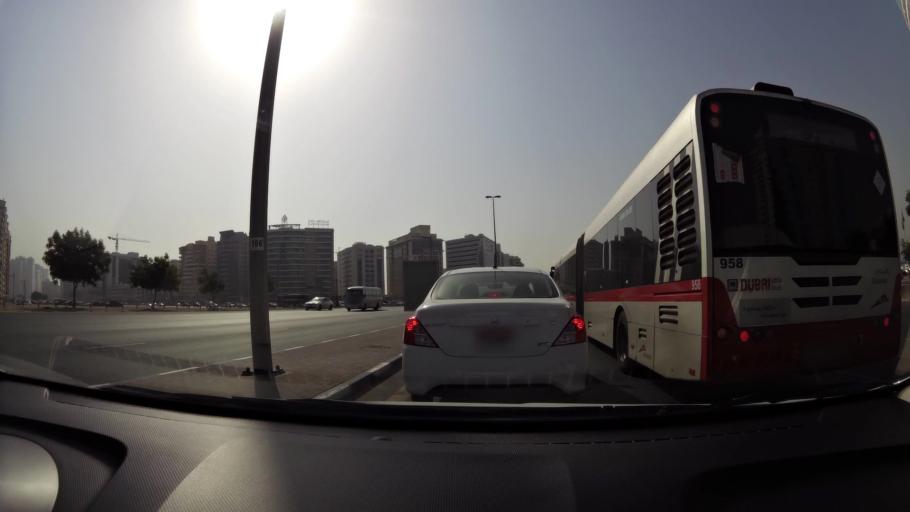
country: AE
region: Ash Shariqah
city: Sharjah
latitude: 25.2886
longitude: 55.3654
